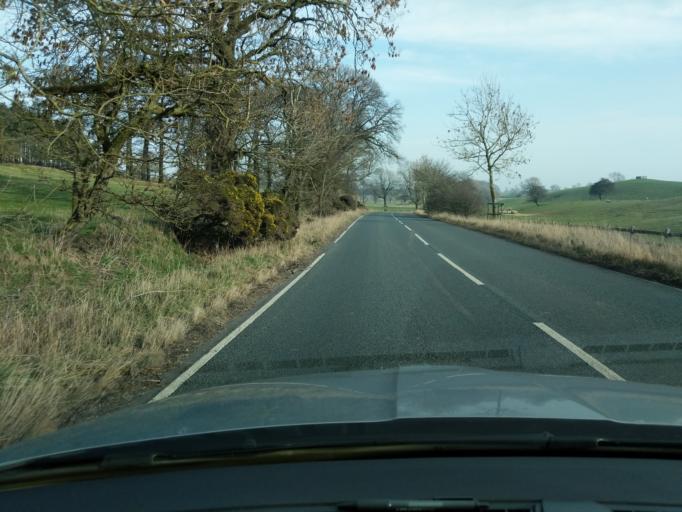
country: GB
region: England
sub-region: North Yorkshire
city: Catterick Garrison
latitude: 54.3475
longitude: -1.7536
